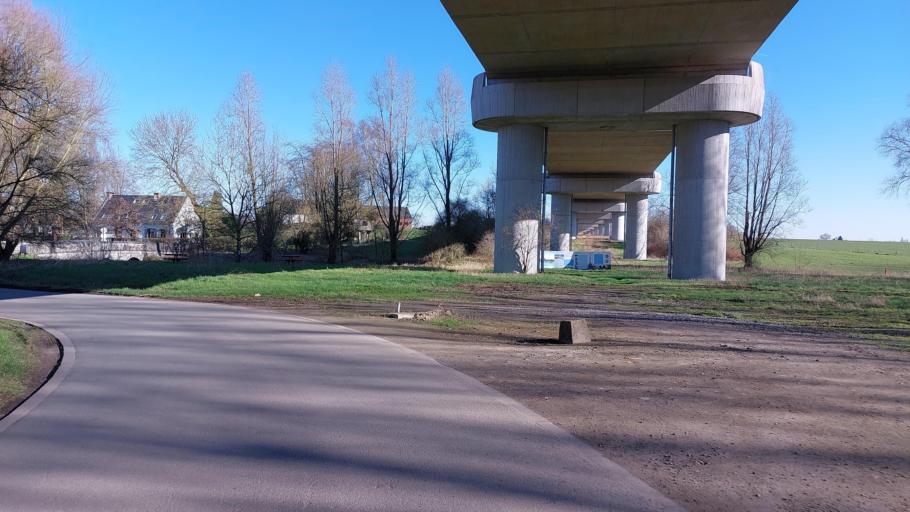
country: BE
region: Wallonia
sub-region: Province du Hainaut
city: Chievres
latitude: 50.6080
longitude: 3.8152
